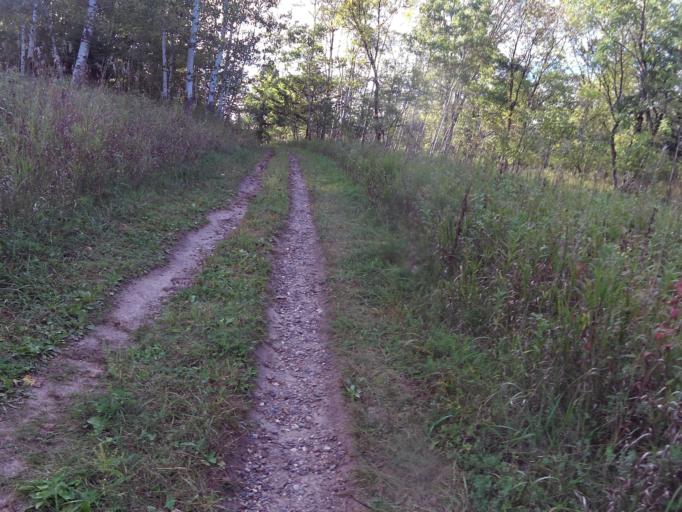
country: US
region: Minnesota
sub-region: Washington County
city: Afton
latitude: 44.8609
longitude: -92.7975
